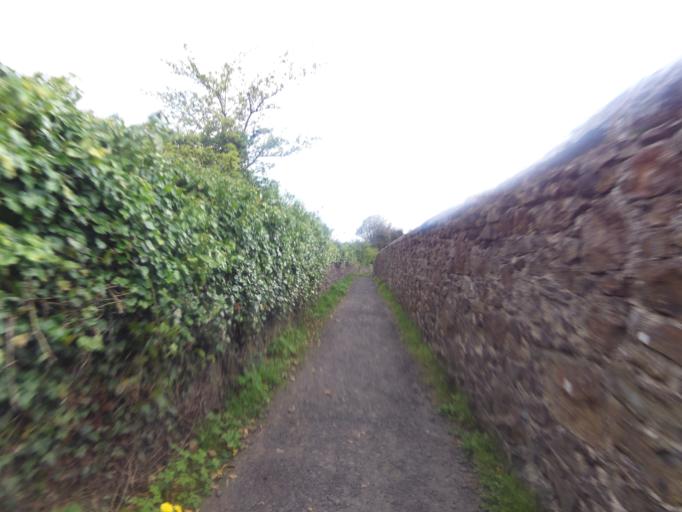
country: GB
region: Scotland
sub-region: Fife
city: Burntisland
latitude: 56.0605
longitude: -3.2551
